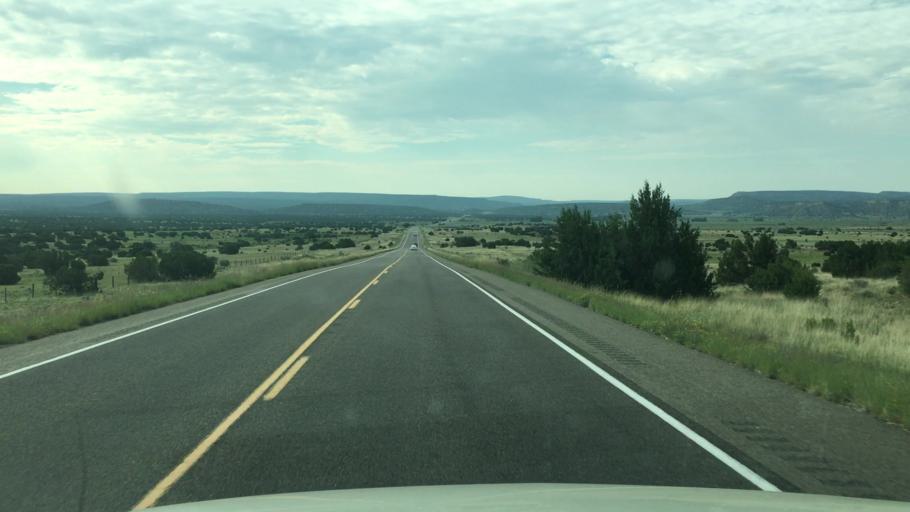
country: US
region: New Mexico
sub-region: Santa Fe County
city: Eldorado at Santa Fe
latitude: 35.4257
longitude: -105.8764
